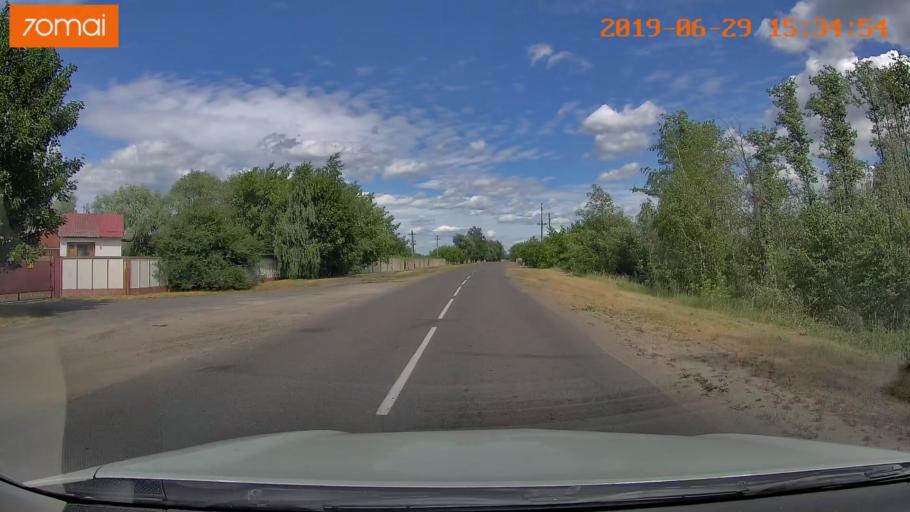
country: BY
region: Brest
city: Mikashevichy
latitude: 52.2148
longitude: 27.4634
